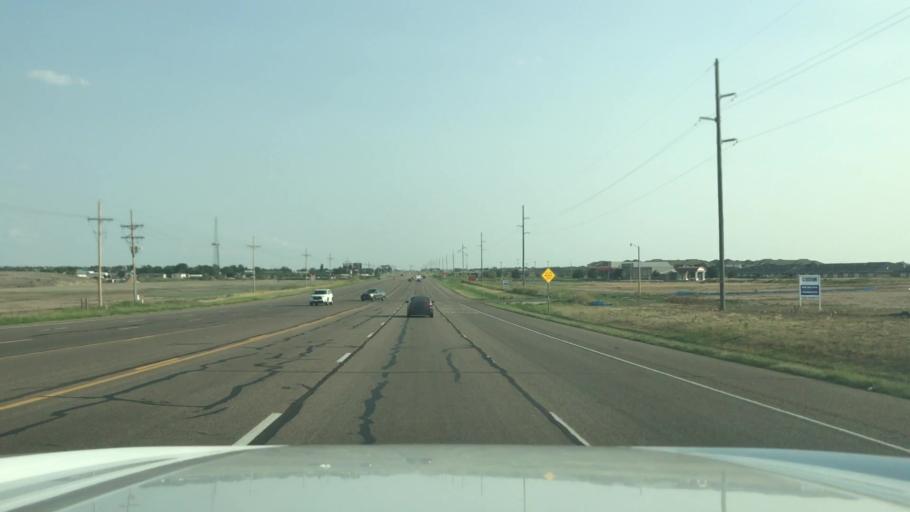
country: US
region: Texas
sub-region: Potter County
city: Amarillo
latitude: 35.1380
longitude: -101.9382
